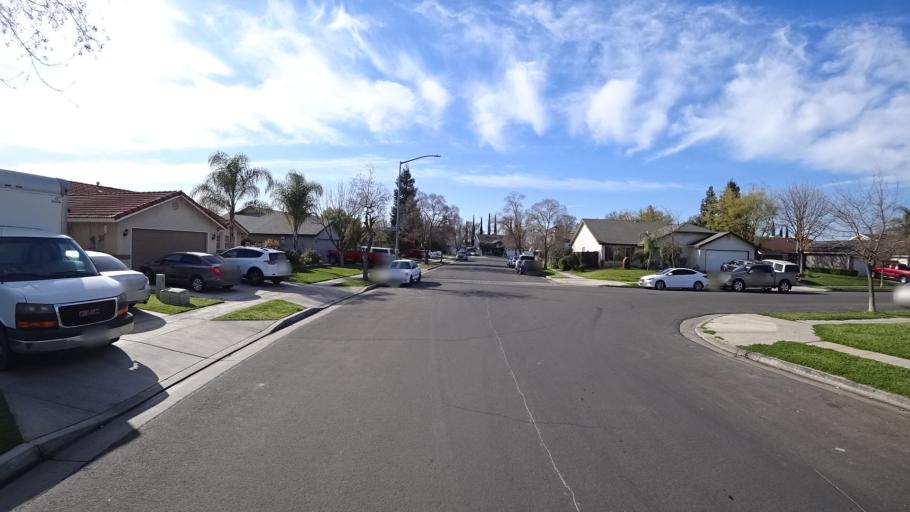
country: US
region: California
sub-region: Fresno County
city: West Park
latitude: 36.8038
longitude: -119.8924
